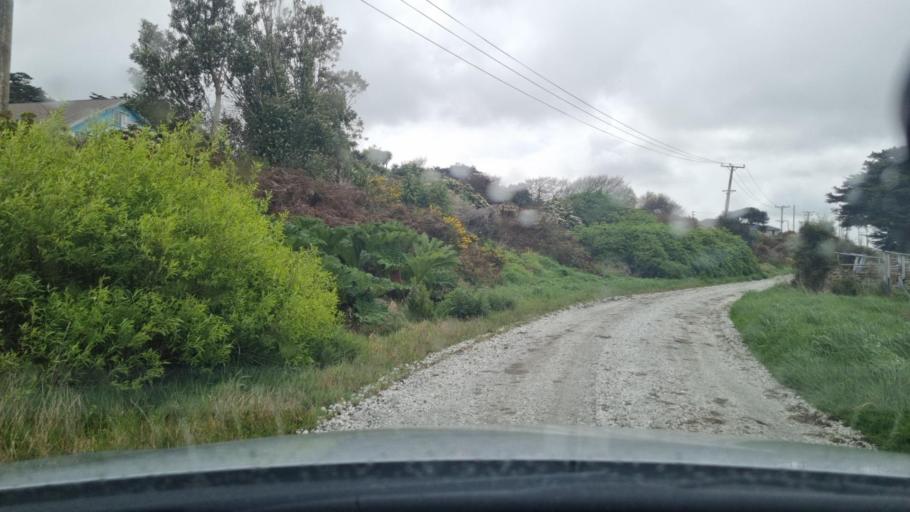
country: NZ
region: Southland
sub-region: Invercargill City
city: Bluff
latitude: -46.5871
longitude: 168.3021
